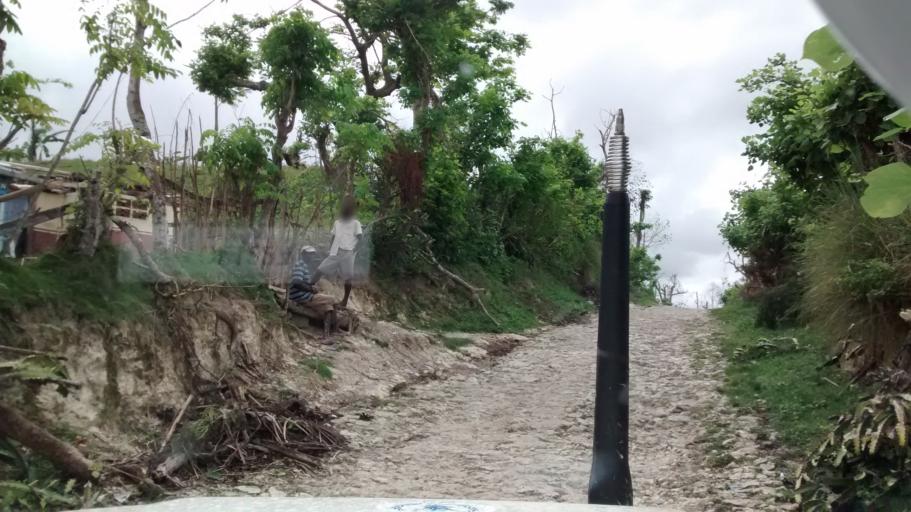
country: HT
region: Grandans
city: Jeremie
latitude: 18.5847
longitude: -74.1465
